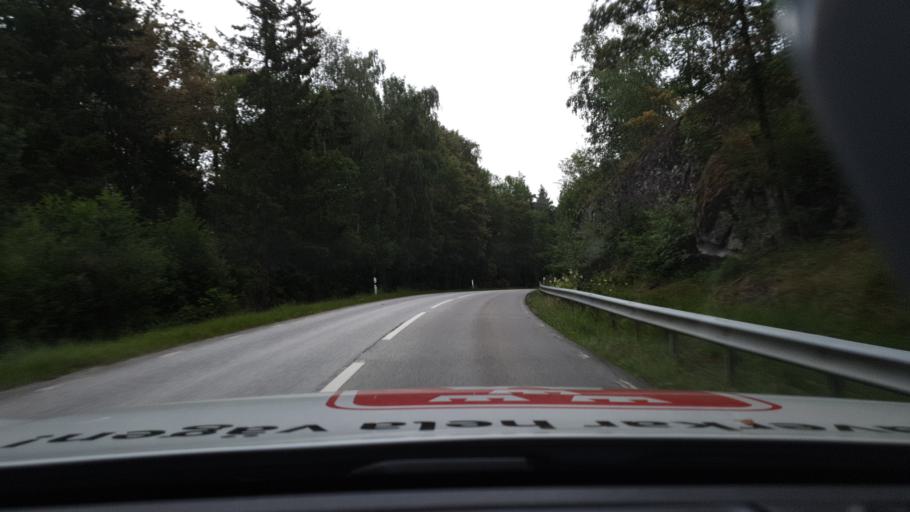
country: SE
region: Stockholm
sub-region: Osterakers Kommun
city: Akersberga
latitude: 59.5041
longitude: 18.3556
